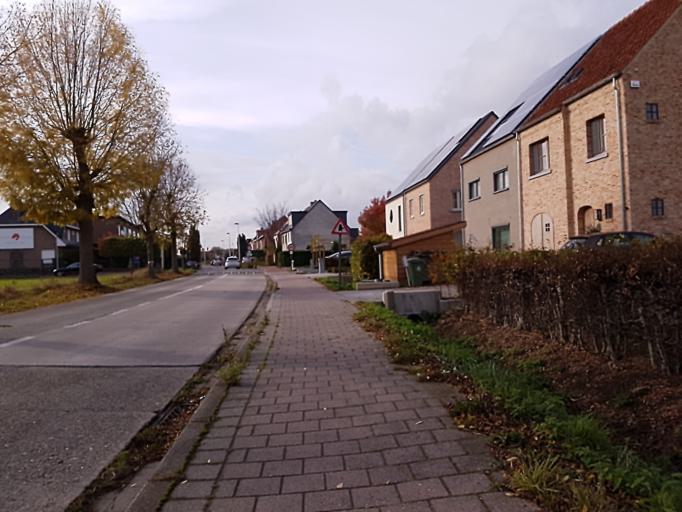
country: BE
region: Flanders
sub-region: Provincie Antwerpen
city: Boechout
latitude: 51.1606
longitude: 4.5133
